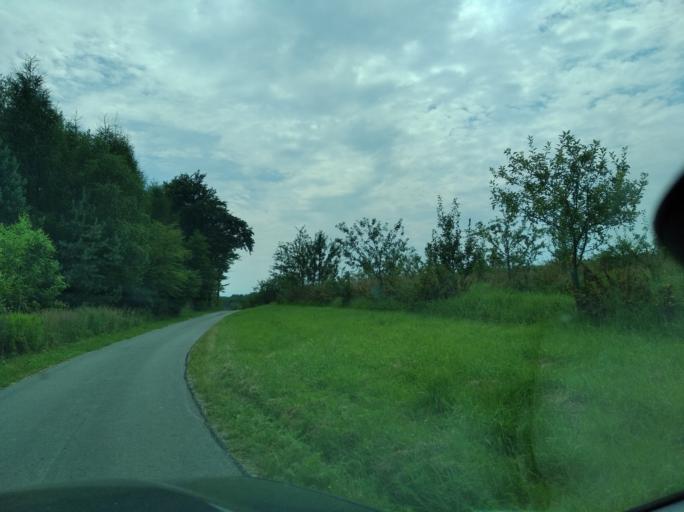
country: PL
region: Subcarpathian Voivodeship
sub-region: Powiat przeworski
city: Lopuszka Wielka
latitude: 49.9033
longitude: 22.4112
